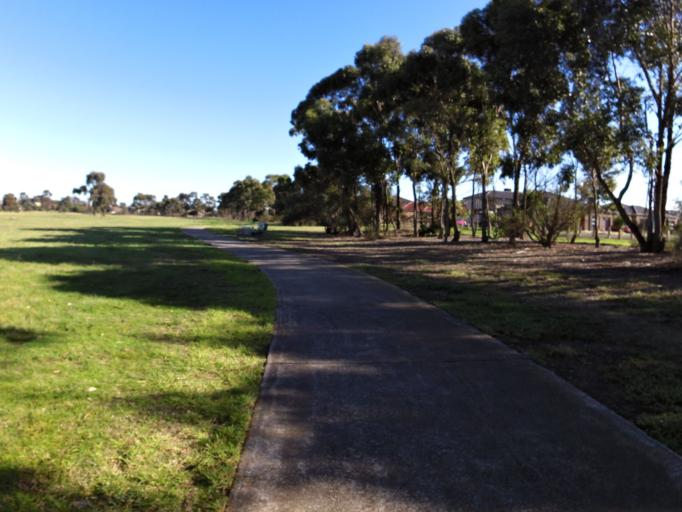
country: AU
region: Victoria
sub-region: Wyndham
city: Tarneit
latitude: -37.8826
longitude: 144.6720
